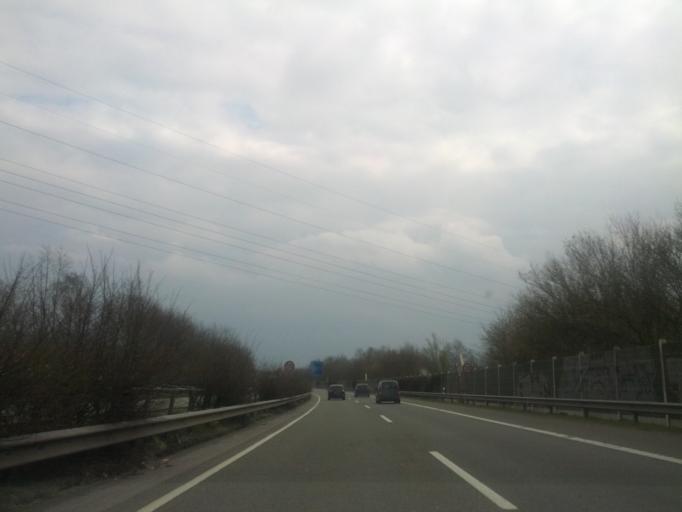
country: DE
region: Lower Saxony
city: Westerstede
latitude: 53.2548
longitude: 7.9512
